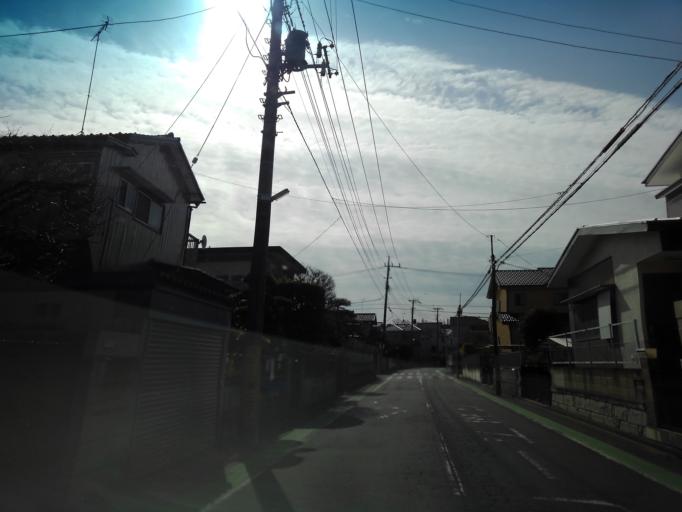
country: JP
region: Saitama
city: Tokorozawa
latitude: 35.7871
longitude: 139.5125
